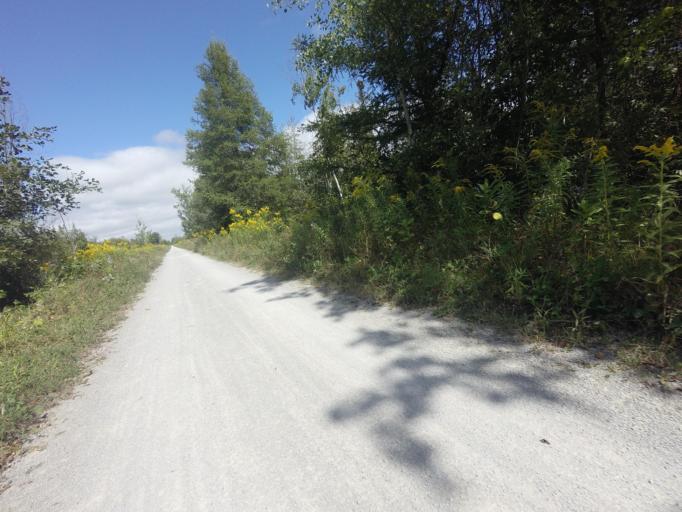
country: CA
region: Ontario
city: Uxbridge
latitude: 44.1343
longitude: -79.0939
